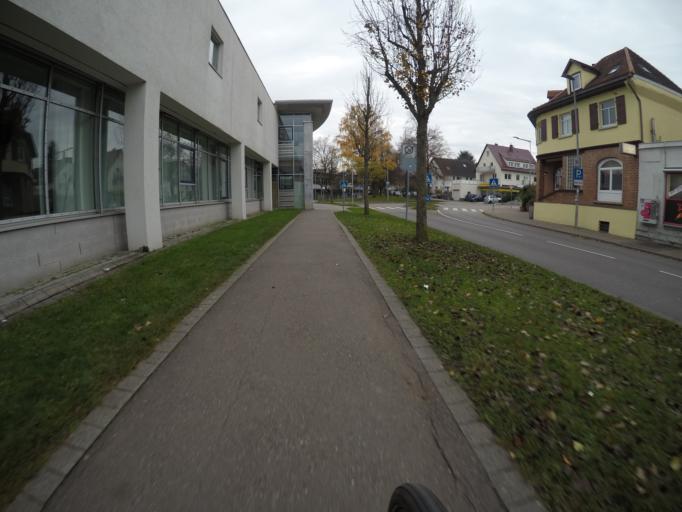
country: DE
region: Baden-Wuerttemberg
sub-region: Regierungsbezirk Stuttgart
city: Leinfelden-Echterdingen
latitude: 48.6945
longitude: 9.1428
